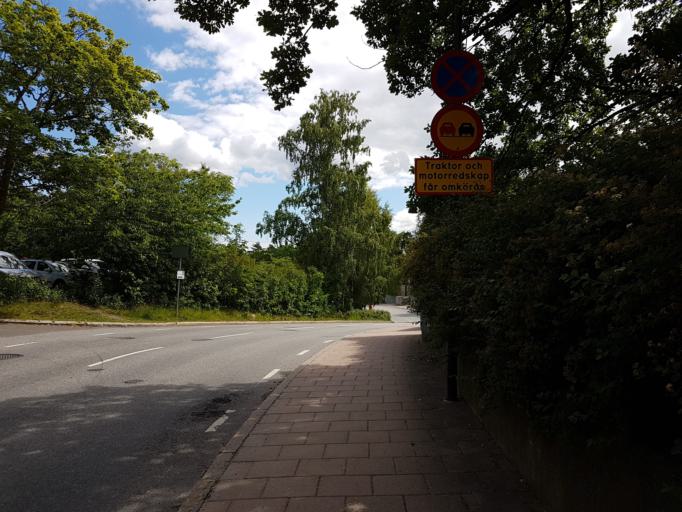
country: SE
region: Stockholm
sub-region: Lidingo
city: Lidingoe
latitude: 59.3596
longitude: 18.1219
